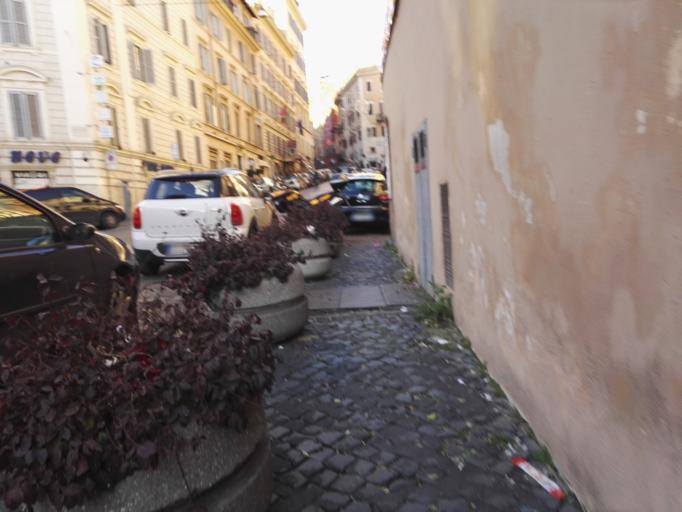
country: IT
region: Latium
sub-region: Citta metropolitana di Roma Capitale
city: Rome
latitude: 41.9038
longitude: 12.4855
